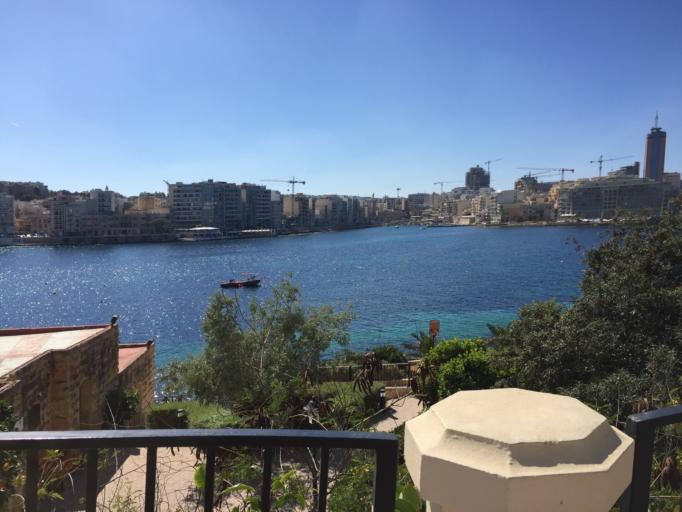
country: MT
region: Tas-Sliema
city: Sliema
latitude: 35.9160
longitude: 14.4982
